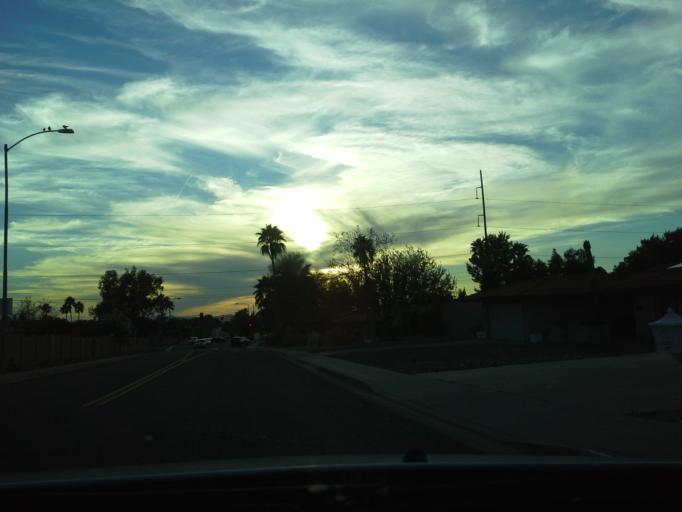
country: US
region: Arizona
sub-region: Maricopa County
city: Glendale
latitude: 33.6258
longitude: -112.0639
